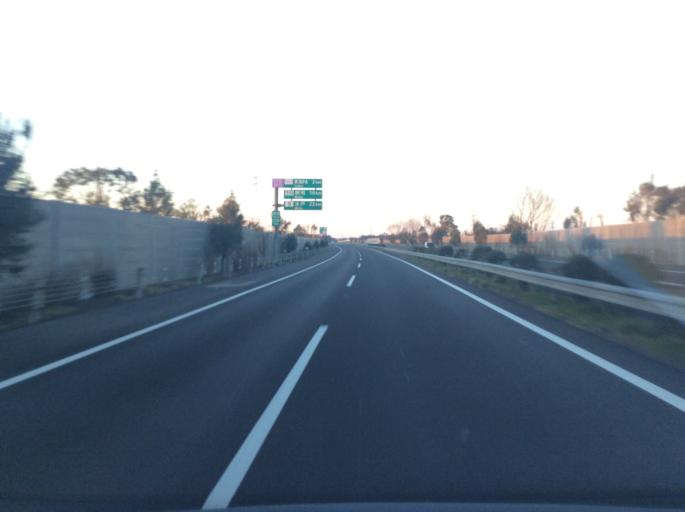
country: JP
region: Ibaraki
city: Funaishikawa
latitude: 36.5003
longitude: 140.5668
